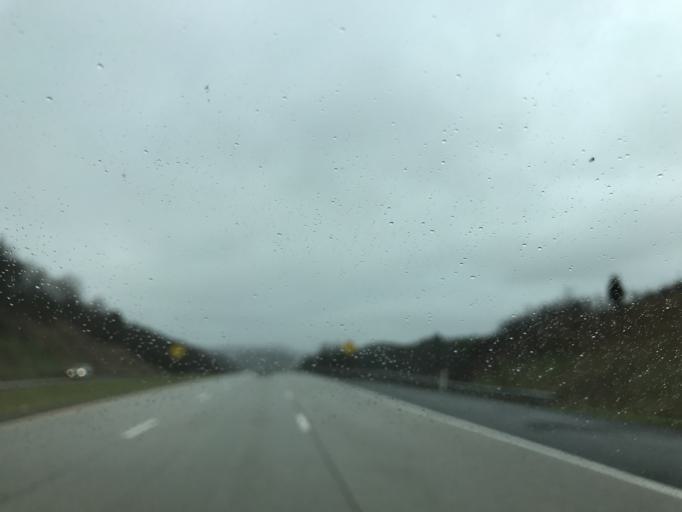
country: US
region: West Virginia
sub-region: Greenbrier County
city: Rainelle
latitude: 37.8395
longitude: -80.7532
